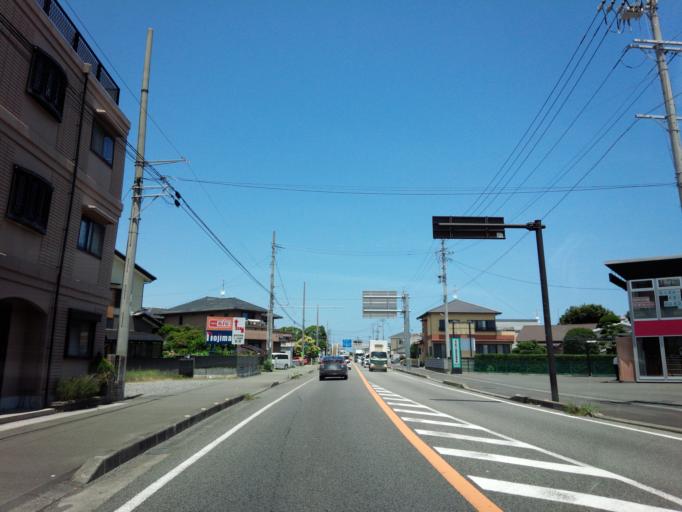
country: JP
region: Shizuoka
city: Shimada
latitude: 34.7749
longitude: 138.2528
